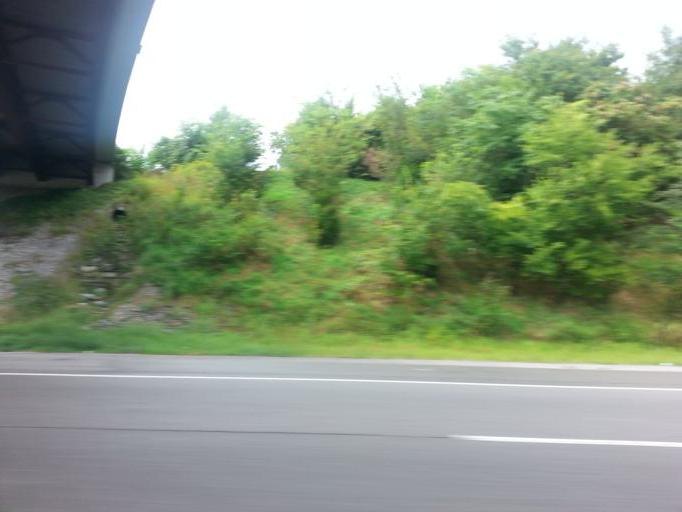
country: US
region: Tennessee
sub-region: Williamson County
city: Nolensville
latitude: 35.8498
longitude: -86.6140
